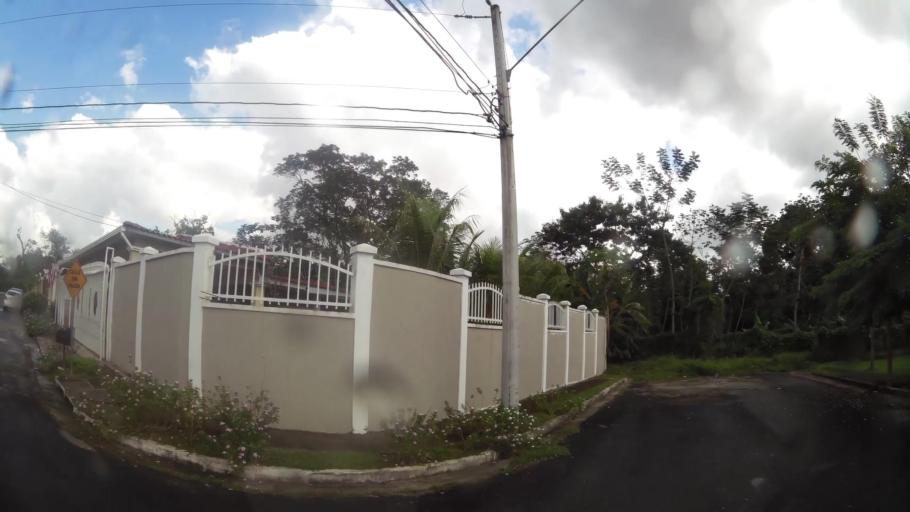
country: PA
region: Panama
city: Nuevo Arraijan
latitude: 8.9403
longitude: -79.7349
